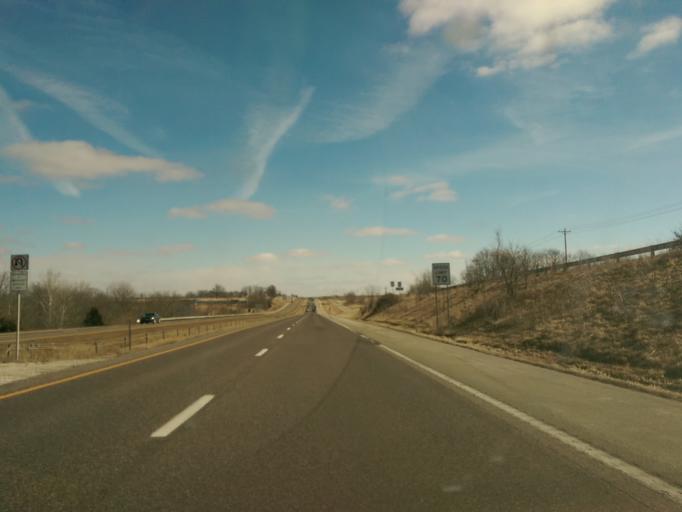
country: US
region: Missouri
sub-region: Callaway County
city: Fulton
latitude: 38.9441
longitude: -91.9304
